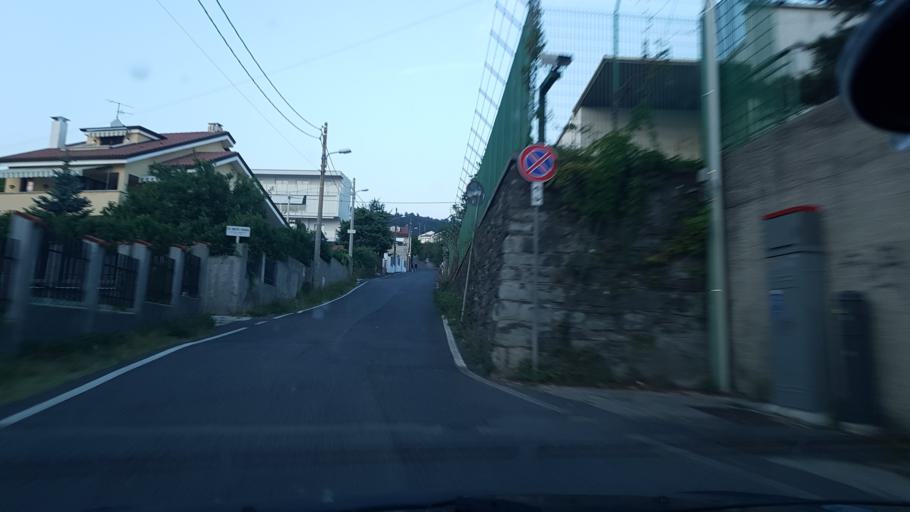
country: IT
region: Friuli Venezia Giulia
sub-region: Provincia di Trieste
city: Villa Opicina
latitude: 45.6745
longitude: 13.7649
